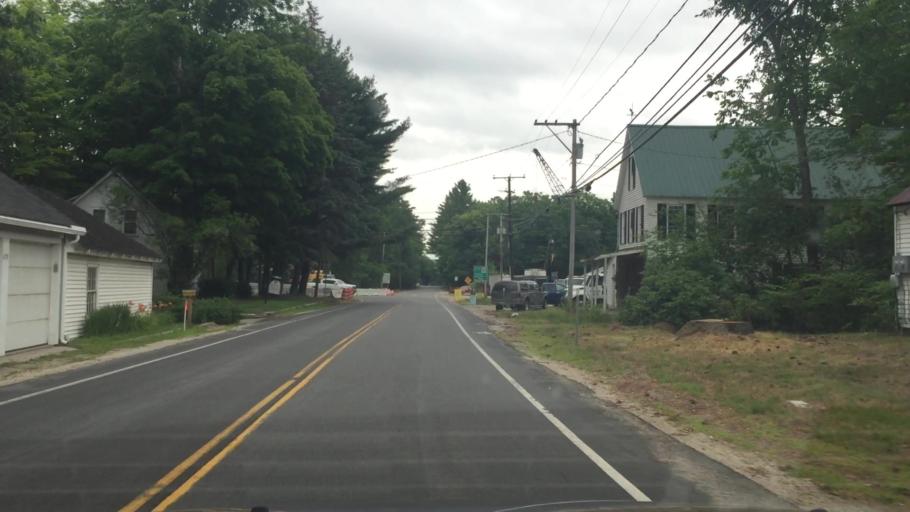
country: US
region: New Hampshire
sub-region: Carroll County
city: Tamworth
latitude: 43.8316
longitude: -71.2678
